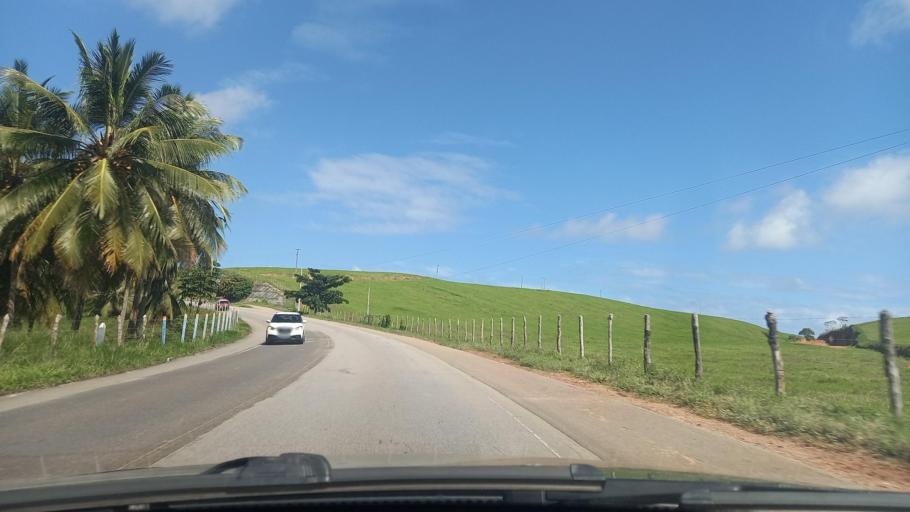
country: BR
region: Alagoas
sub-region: Marechal Deodoro
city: Marechal Deodoro
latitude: -9.8600
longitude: -35.9191
